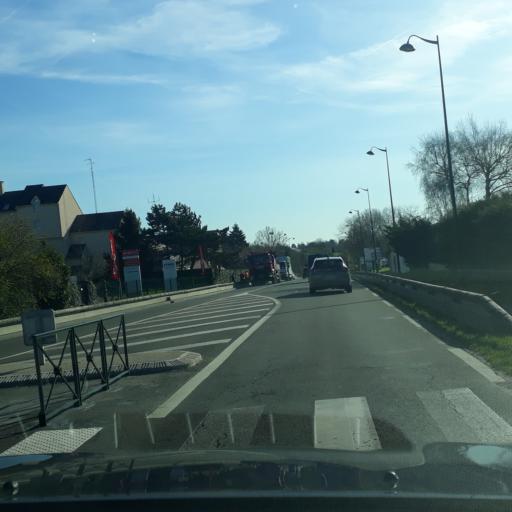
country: FR
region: Ile-de-France
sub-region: Departement de l'Essonne
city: Etampes
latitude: 48.4409
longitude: 2.1472
